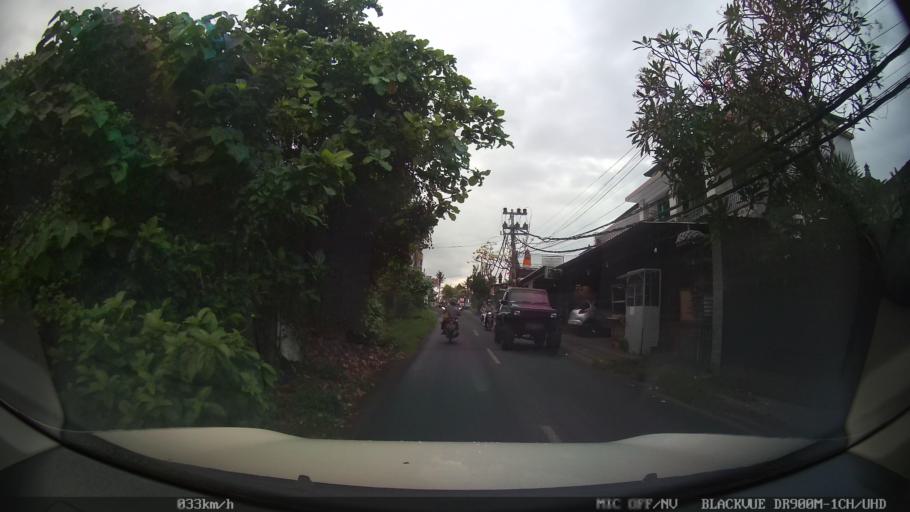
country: ID
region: Bali
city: Banjar Paangkelod
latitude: -8.6191
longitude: 115.2558
